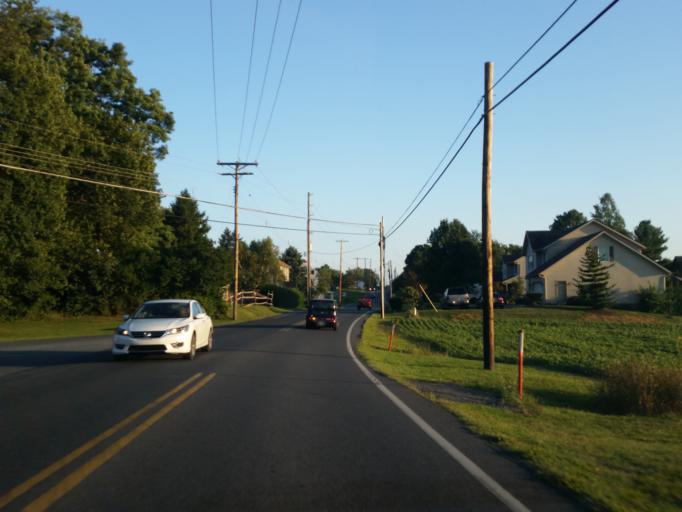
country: US
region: Pennsylvania
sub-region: Lebanon County
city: Sand Hill
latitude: 40.3702
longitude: -76.4326
